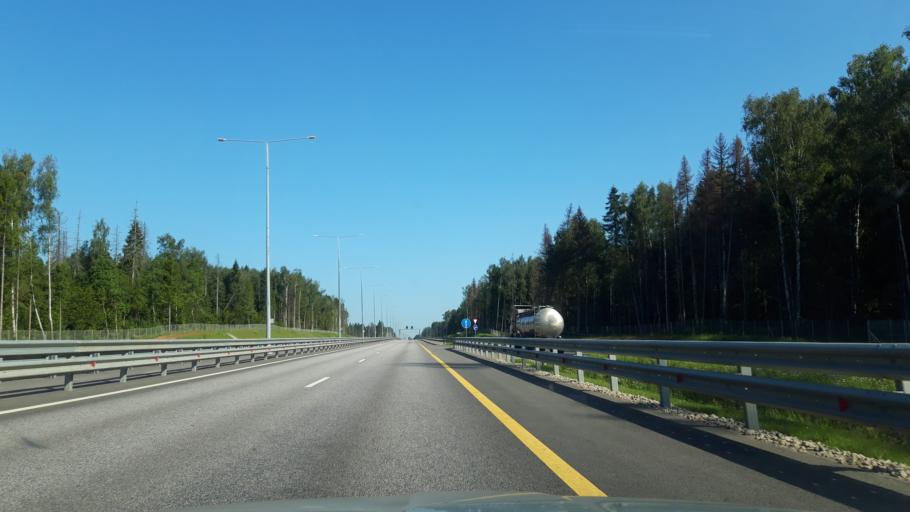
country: RU
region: Moskovskaya
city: Klin
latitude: 56.2523
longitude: 36.7392
